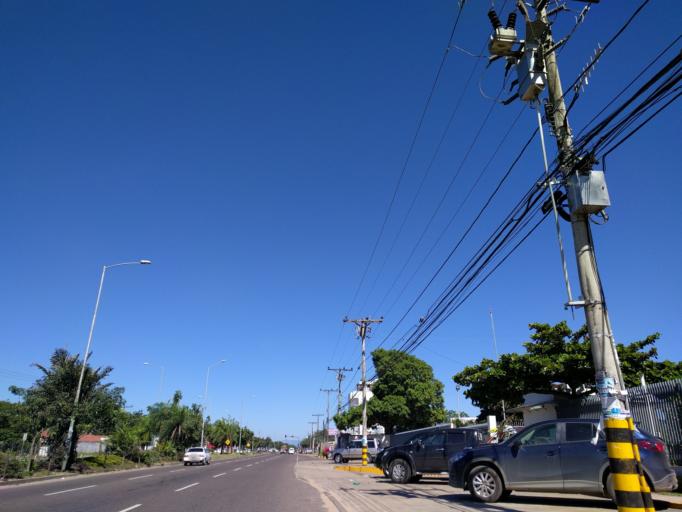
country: BO
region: Santa Cruz
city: Santa Cruz de la Sierra
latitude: -17.8146
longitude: -63.2115
